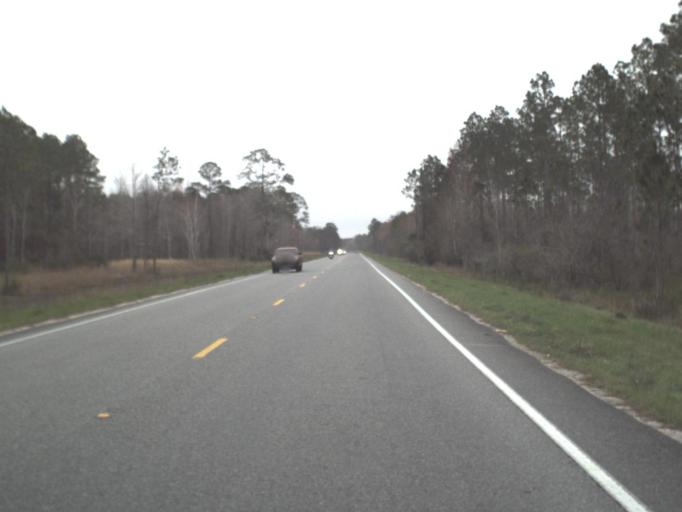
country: US
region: Florida
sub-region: Leon County
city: Woodville
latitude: 30.1943
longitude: -84.1313
